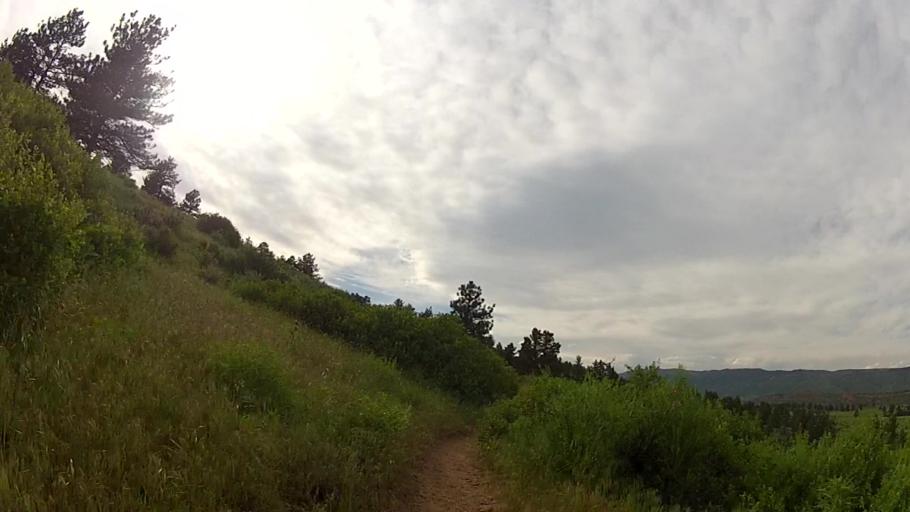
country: US
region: Colorado
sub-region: Larimer County
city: Laporte
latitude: 40.4801
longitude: -105.2369
